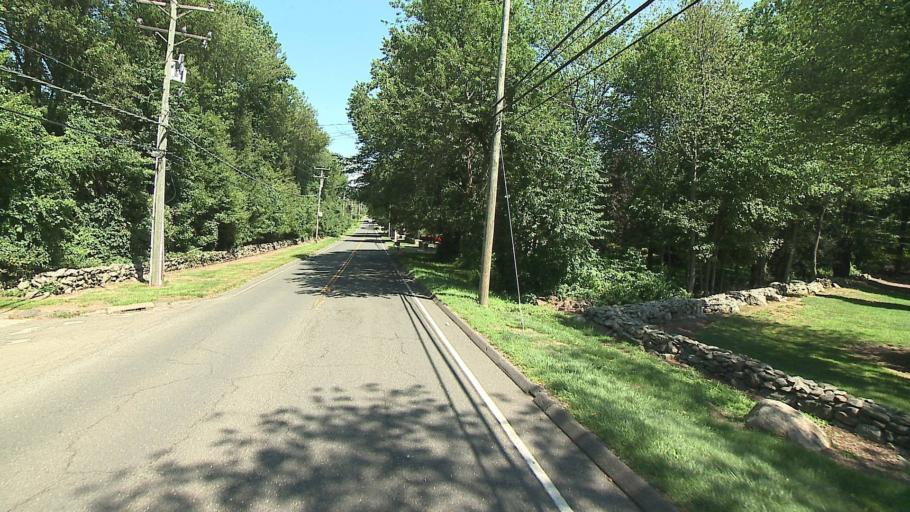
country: US
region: Connecticut
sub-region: Fairfield County
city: Trumbull
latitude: 41.3352
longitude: -73.2057
